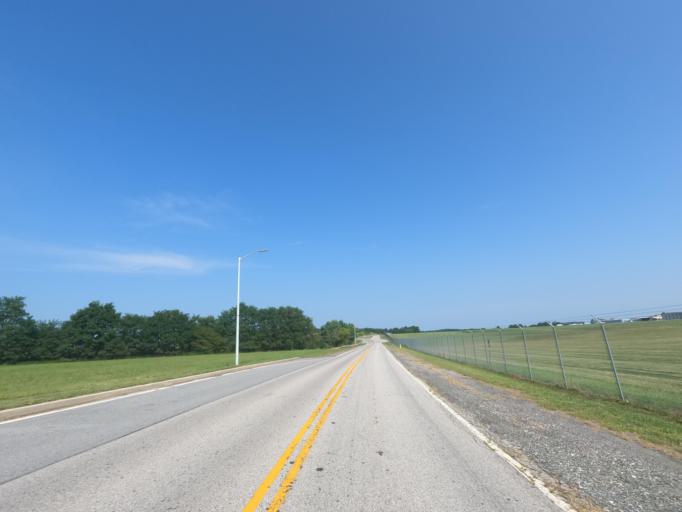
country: US
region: Maryland
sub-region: Carroll County
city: Westminster
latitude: 39.5998
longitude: -77.0039
